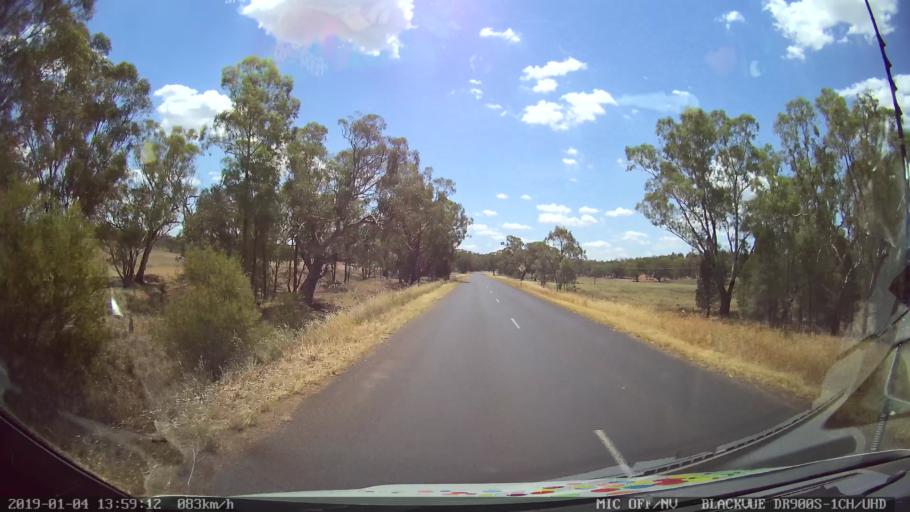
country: AU
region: New South Wales
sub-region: Dubbo Municipality
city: Dubbo
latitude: -32.3199
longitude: 148.5910
